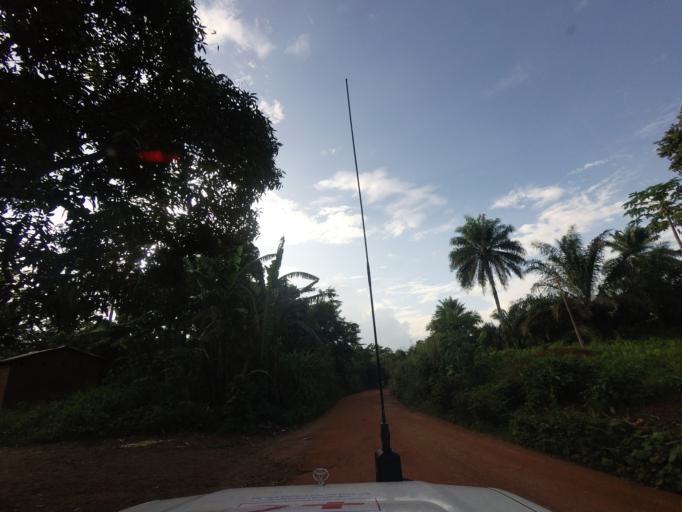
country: GN
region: Nzerekore
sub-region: Nzerekore Prefecture
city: Nzerekore
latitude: 7.6735
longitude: -8.8112
